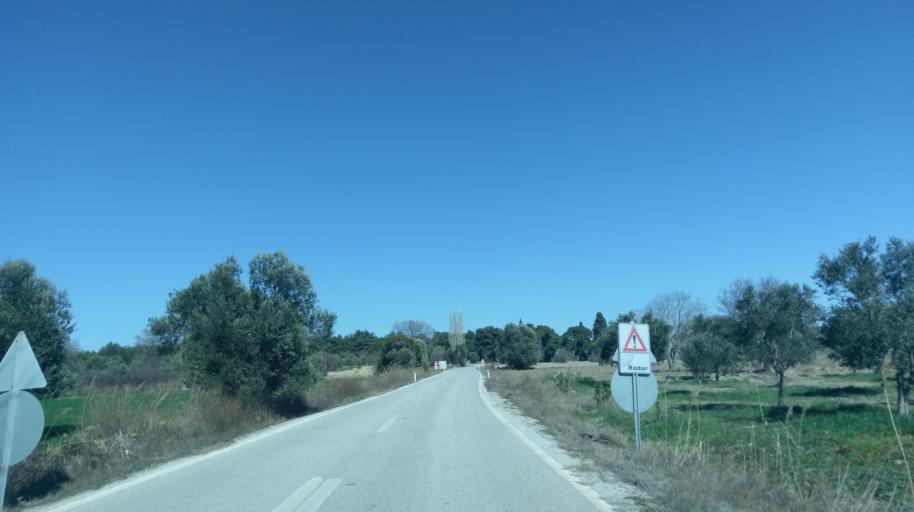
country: TR
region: Canakkale
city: Intepe
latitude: 40.0573
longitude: 26.1974
